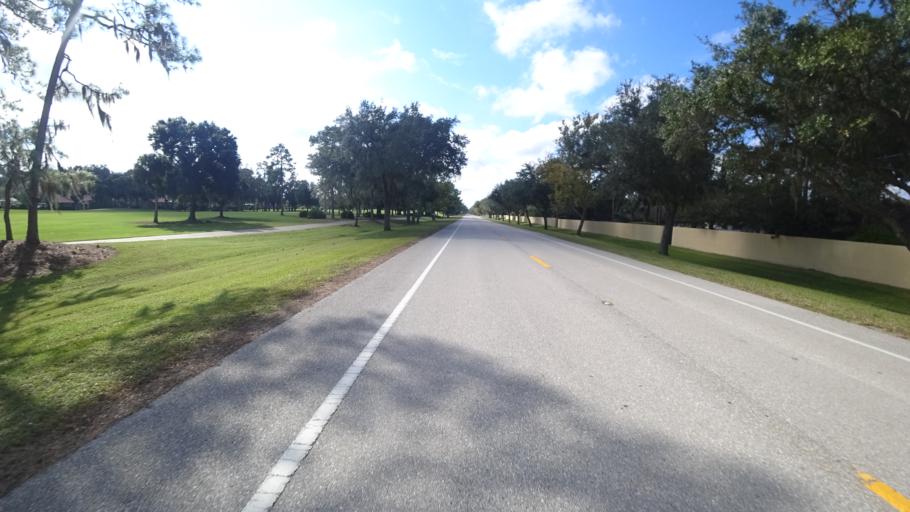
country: US
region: Florida
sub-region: Sarasota County
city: Desoto Lakes
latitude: 27.4017
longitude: -82.4871
